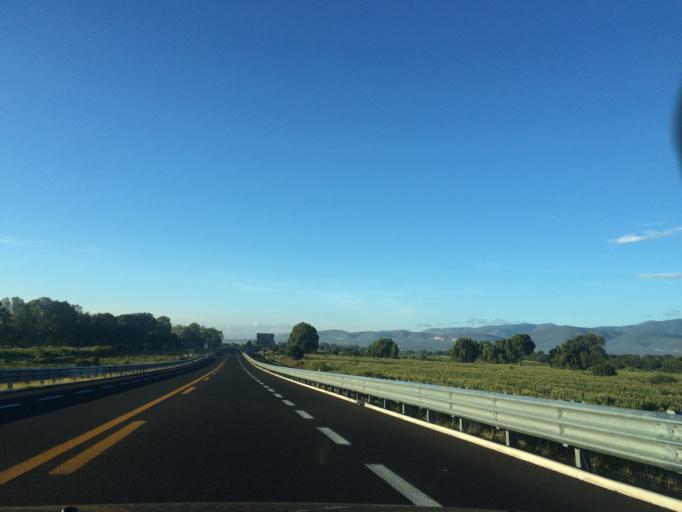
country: MX
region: Puebla
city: Santiago Miahuatlan
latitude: 18.5308
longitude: -97.4572
